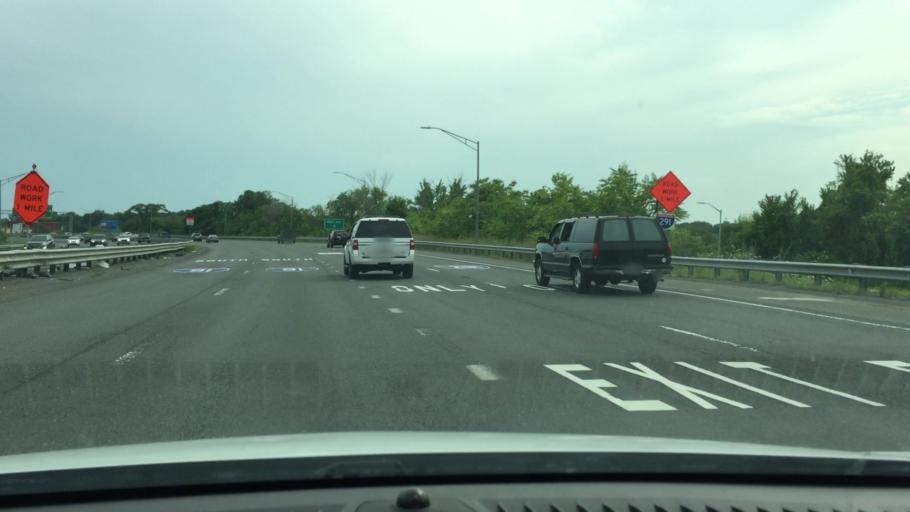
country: US
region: Massachusetts
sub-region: Hampden County
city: West Springfield
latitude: 42.1213
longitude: -72.6092
